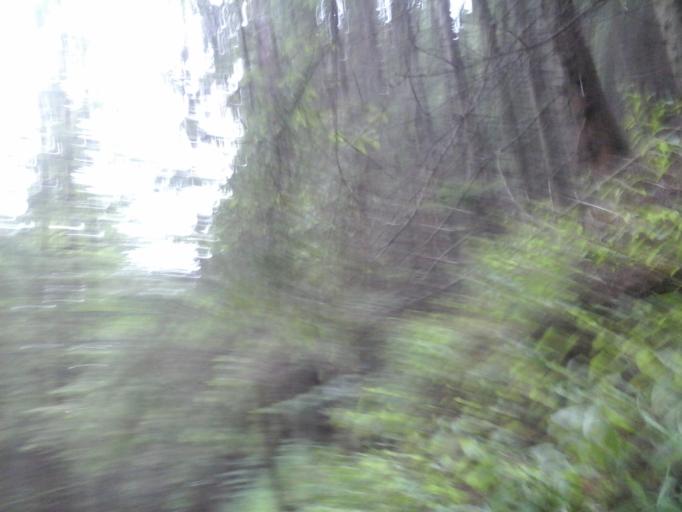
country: PL
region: Lesser Poland Voivodeship
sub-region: Powiat tatrzanski
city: Zakopane
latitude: 49.2686
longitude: 19.9873
